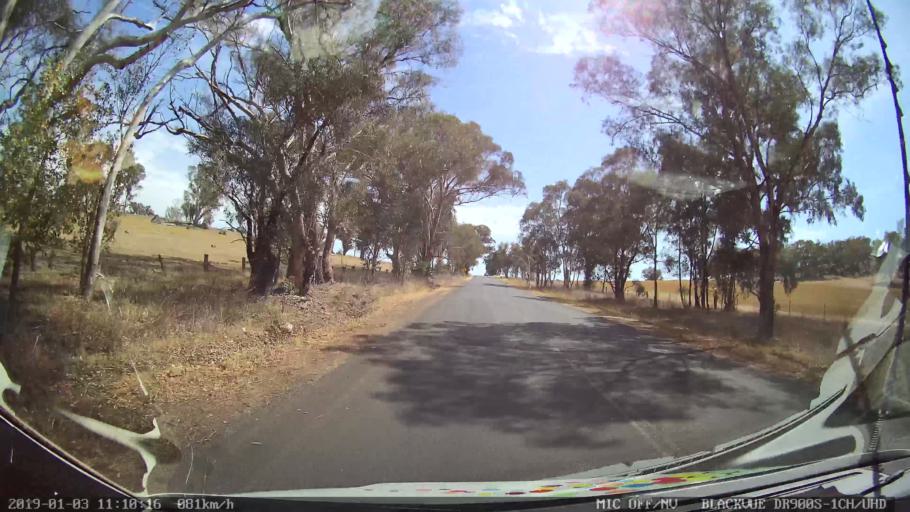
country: AU
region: New South Wales
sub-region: Young
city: Young
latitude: -34.2287
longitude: 148.2579
